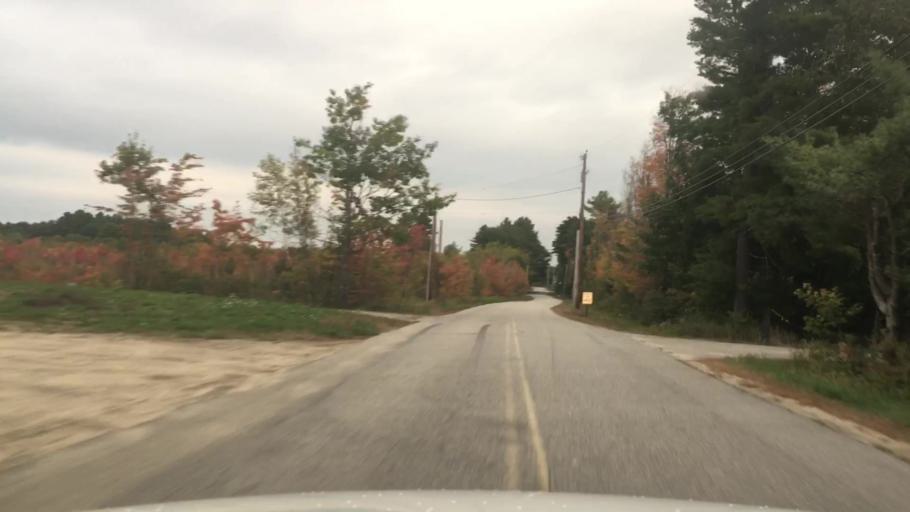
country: US
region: Maine
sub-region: York County
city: Buxton
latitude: 43.6419
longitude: -70.5269
